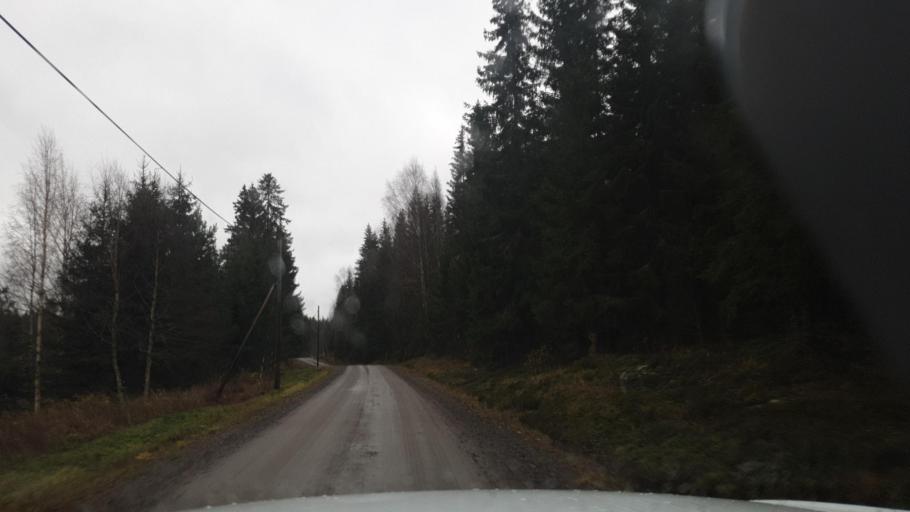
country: SE
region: Vaermland
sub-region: Eda Kommun
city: Charlottenberg
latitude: 59.9203
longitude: 12.3784
